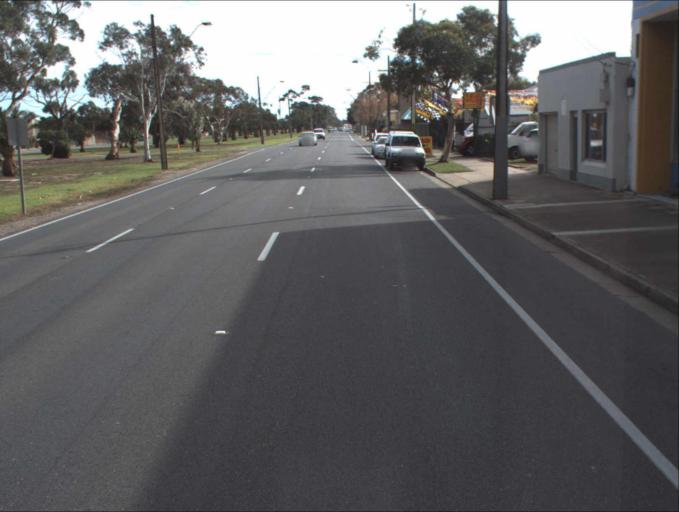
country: AU
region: South Australia
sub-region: Port Adelaide Enfield
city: Cheltenham
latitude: -34.8670
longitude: 138.5176
